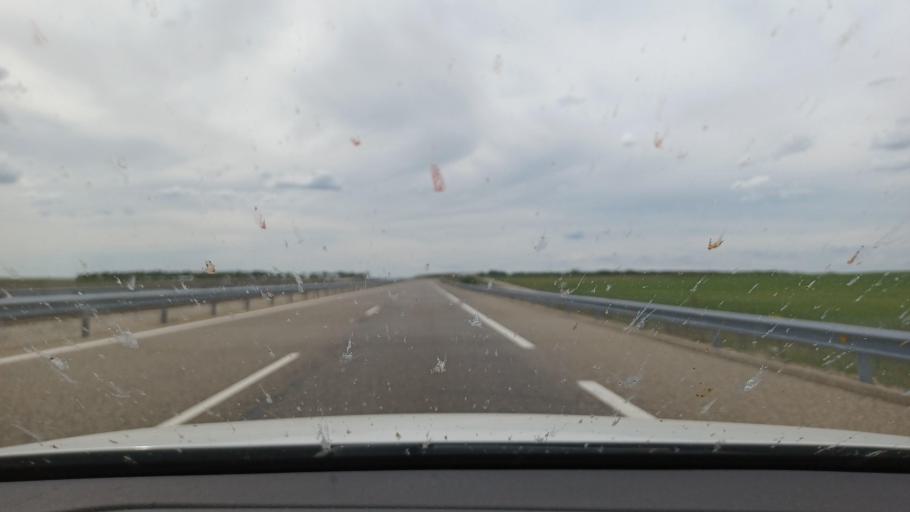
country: ES
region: Castille and Leon
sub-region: Provincia de Valladolid
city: San Miguel del Arroyo
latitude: 41.4311
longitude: -4.4498
